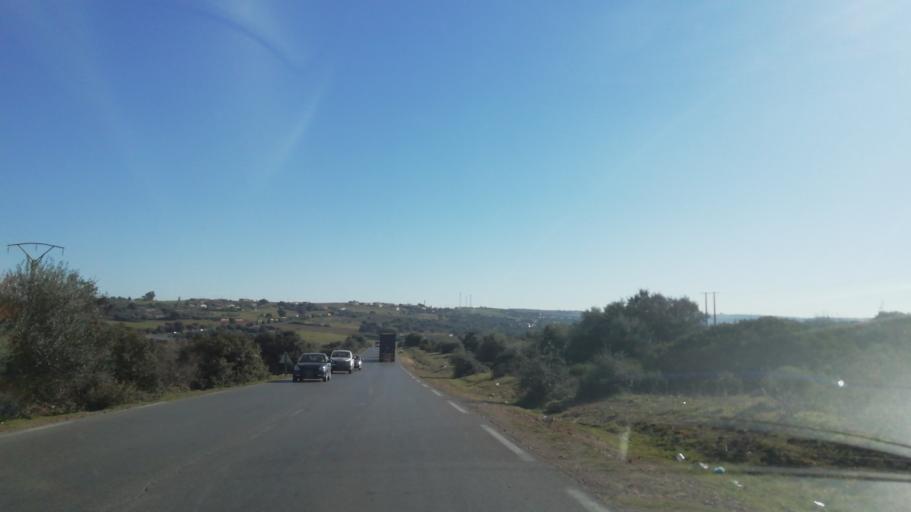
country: DZ
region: Relizane
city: Smala
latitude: 35.6886
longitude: 0.7950
